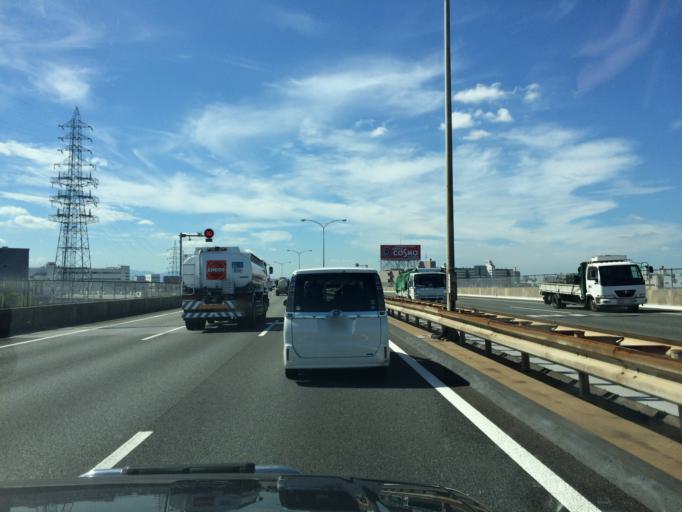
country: JP
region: Osaka
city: Yao
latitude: 34.6279
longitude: 135.5783
